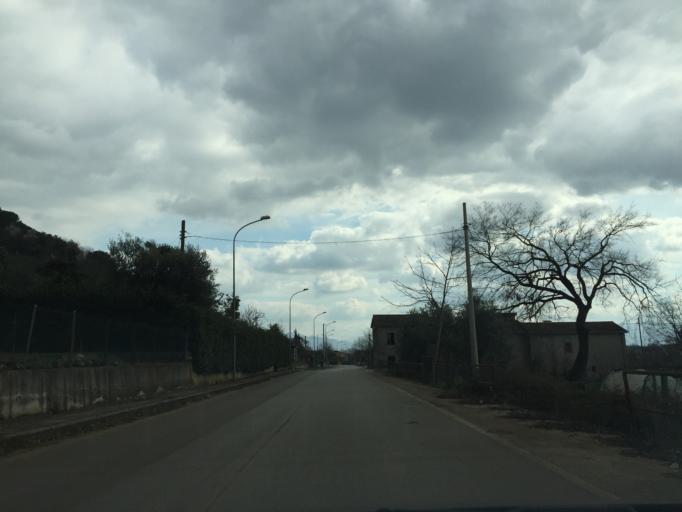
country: IT
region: Latium
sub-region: Provincia di Frosinone
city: Villa Santa Lucia
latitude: 41.4925
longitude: 13.7817
